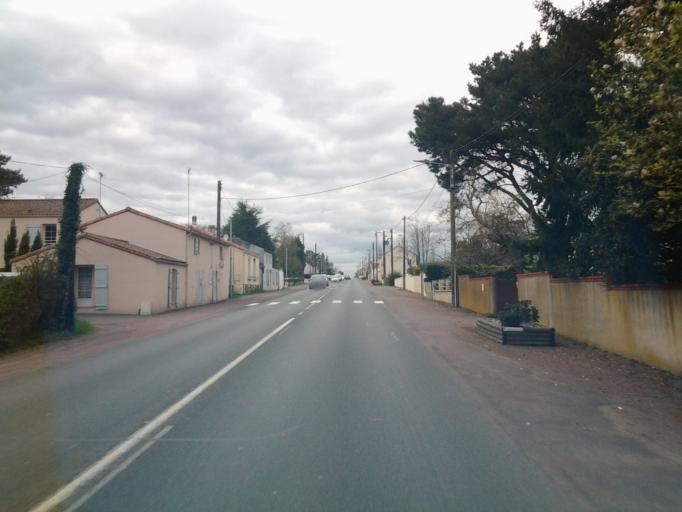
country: FR
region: Pays de la Loire
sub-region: Departement de la Vendee
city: Saint-Florent-des-Bois
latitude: 46.5972
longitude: -1.3219
